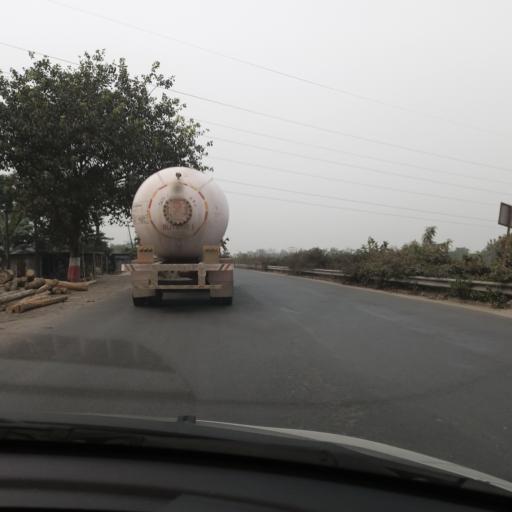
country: IN
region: West Bengal
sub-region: Darjiling
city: Shiliguri
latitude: 26.6570
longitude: 88.4126
